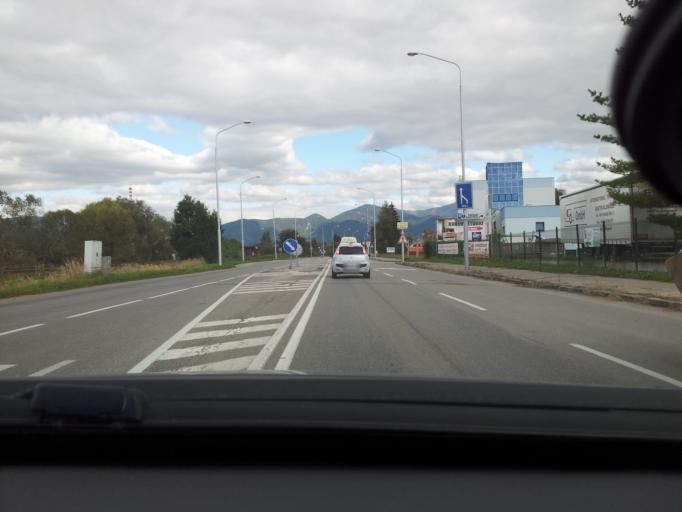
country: SK
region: Zilinsky
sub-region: Okres Martin
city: Martin
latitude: 49.0452
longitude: 18.9106
